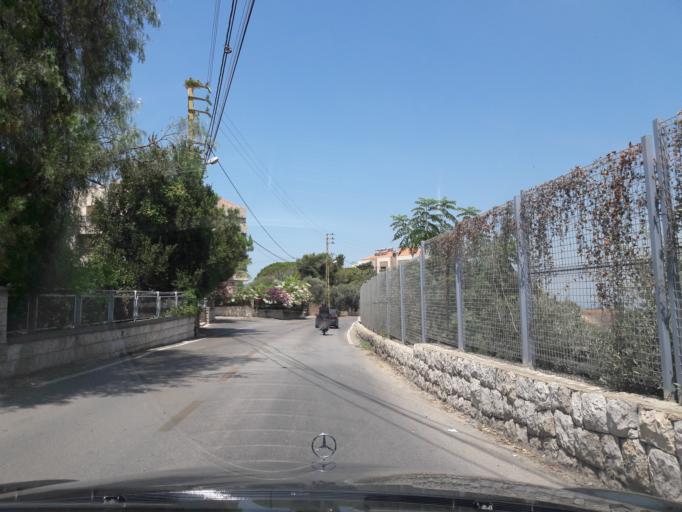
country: LB
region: Mont-Liban
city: Djounie
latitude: 33.9307
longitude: 35.6251
